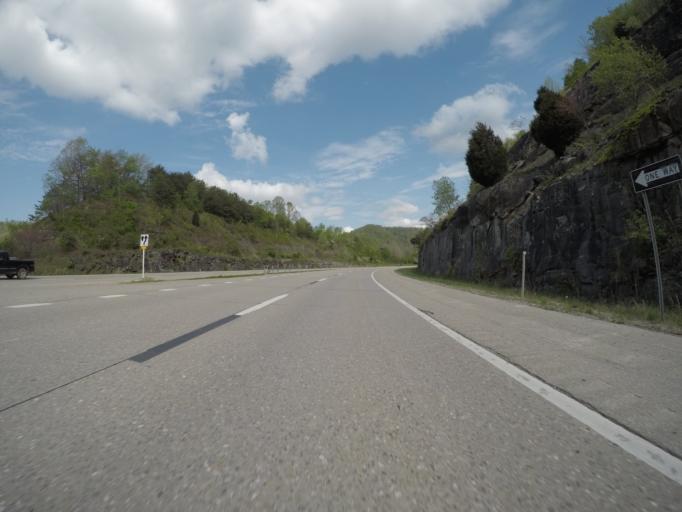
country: US
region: West Virginia
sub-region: Boone County
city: Madison
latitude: 38.1063
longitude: -81.8479
